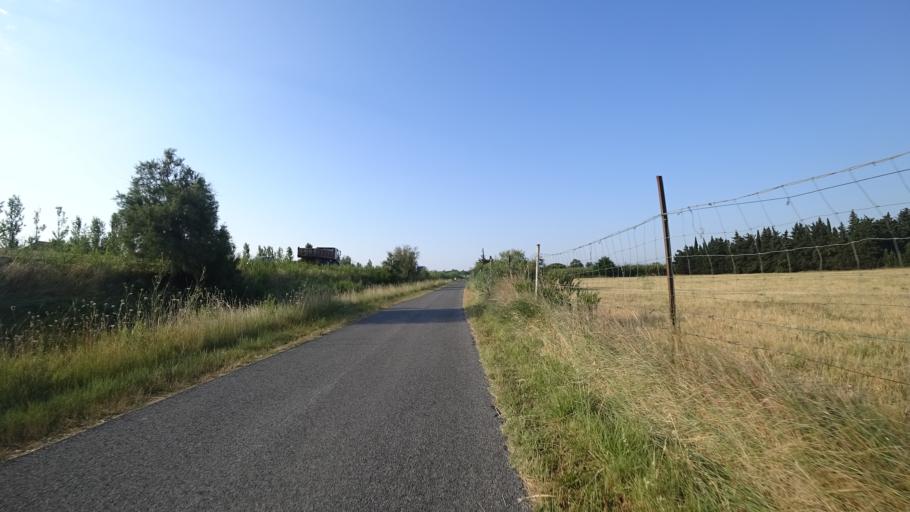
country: FR
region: Languedoc-Roussillon
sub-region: Departement des Pyrenees-Orientales
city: Sainte-Marie-Plage
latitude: 42.7250
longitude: 3.0295
